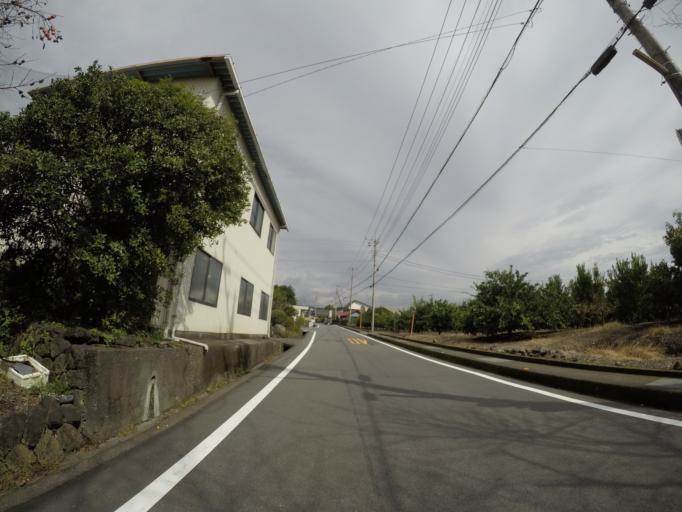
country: JP
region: Shizuoka
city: Fuji
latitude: 35.2063
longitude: 138.6696
